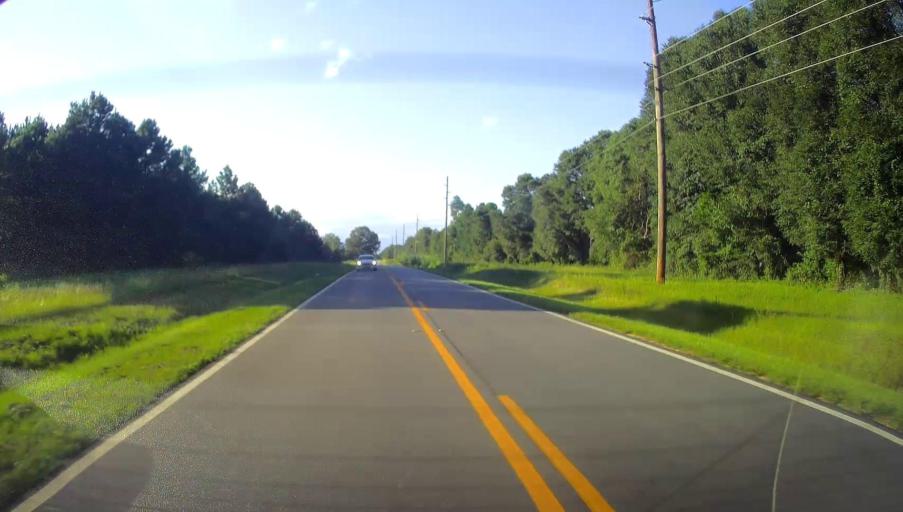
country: US
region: Georgia
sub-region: Pulaski County
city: Hawkinsville
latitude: 32.3074
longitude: -83.4512
